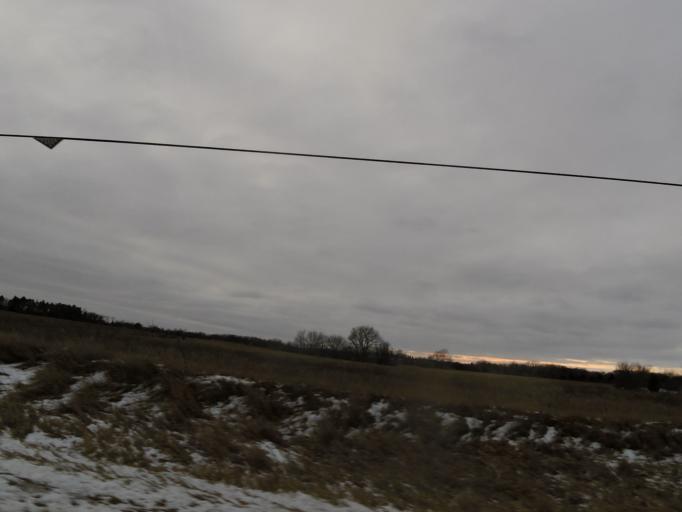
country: US
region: Minnesota
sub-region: Carver County
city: Carver
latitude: 44.7375
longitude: -93.6489
